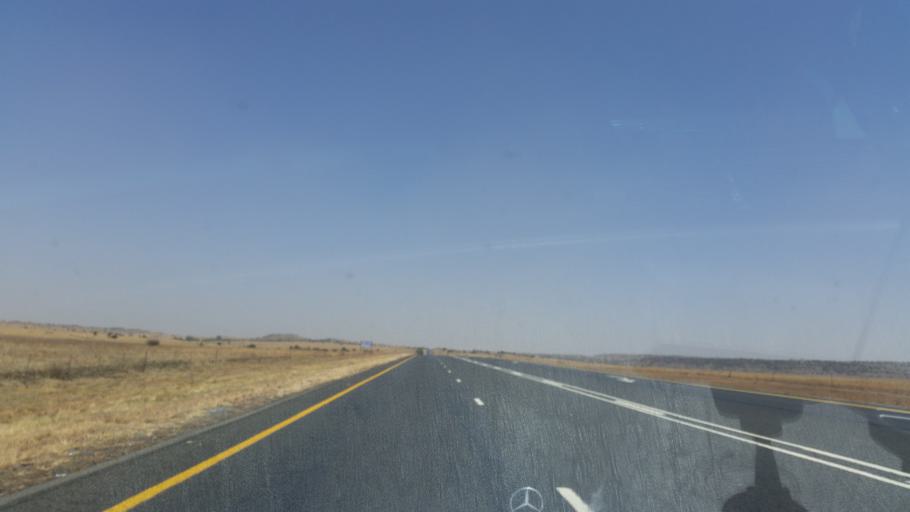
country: ZA
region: Orange Free State
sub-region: Lejweleputswa District Municipality
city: Winburg
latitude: -28.6811
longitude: 26.8293
